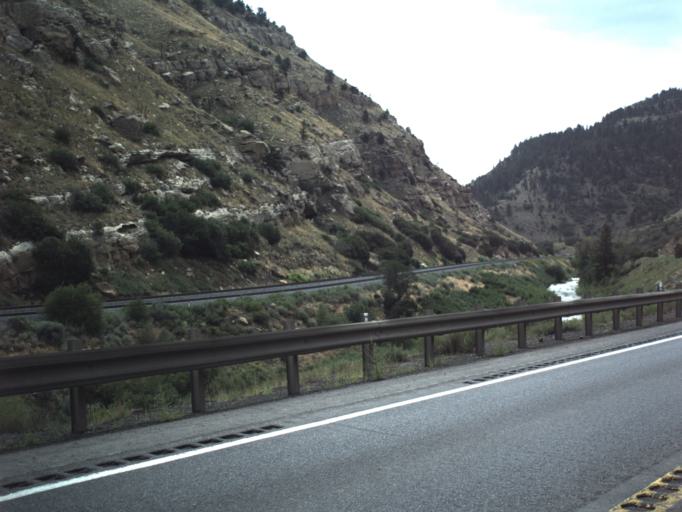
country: US
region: Utah
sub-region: Carbon County
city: Helper
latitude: 39.7700
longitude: -110.9081
